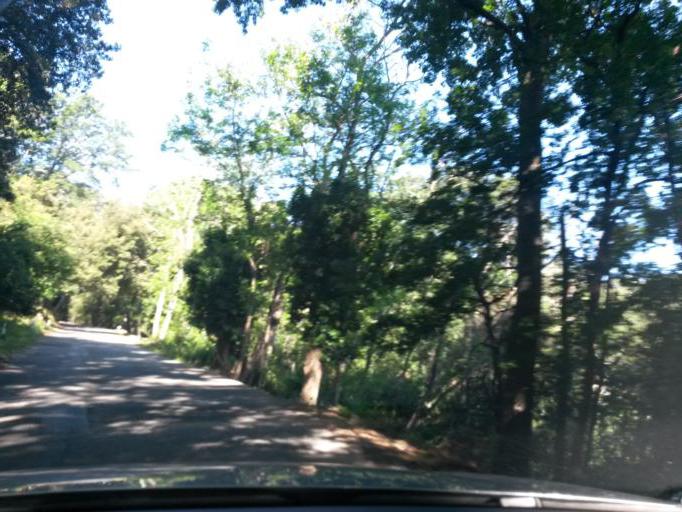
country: IT
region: Tuscany
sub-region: Provincia di Livorno
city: Marciana
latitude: 42.7912
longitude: 10.1779
